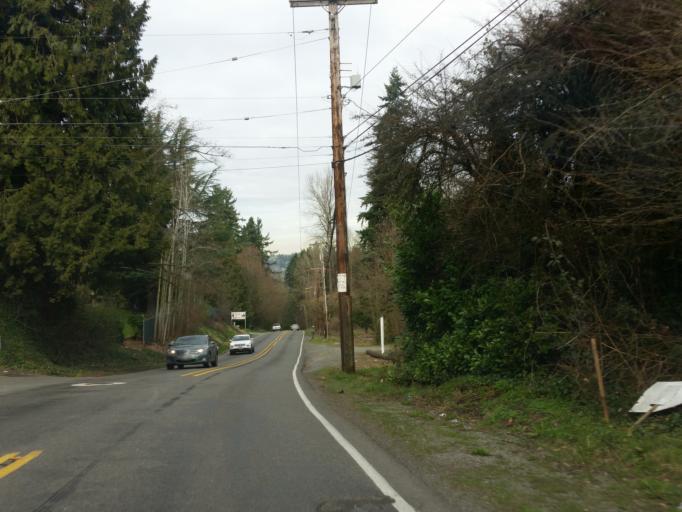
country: US
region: Washington
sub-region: Pierce County
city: Alderton
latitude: 47.1714
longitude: -122.2533
